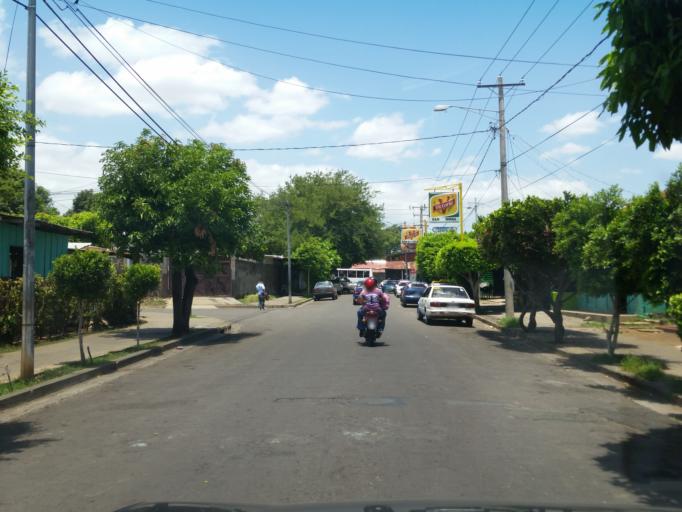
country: NI
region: Managua
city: Managua
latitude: 12.1224
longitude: -86.2428
